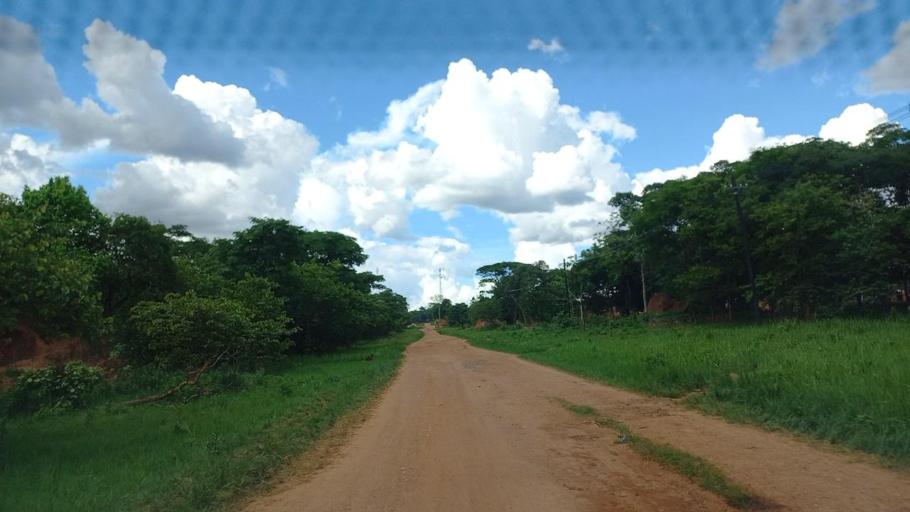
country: ZM
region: North-Western
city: Mwinilunga
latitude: -12.0742
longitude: 24.3010
